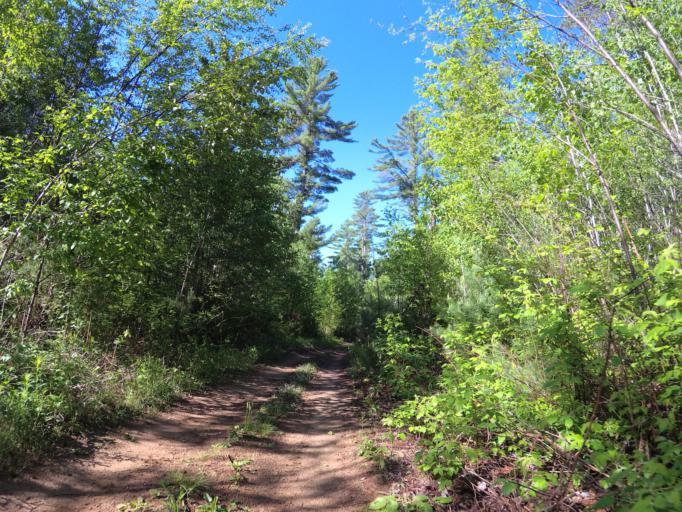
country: CA
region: Ontario
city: Renfrew
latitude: 45.1197
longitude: -77.0352
